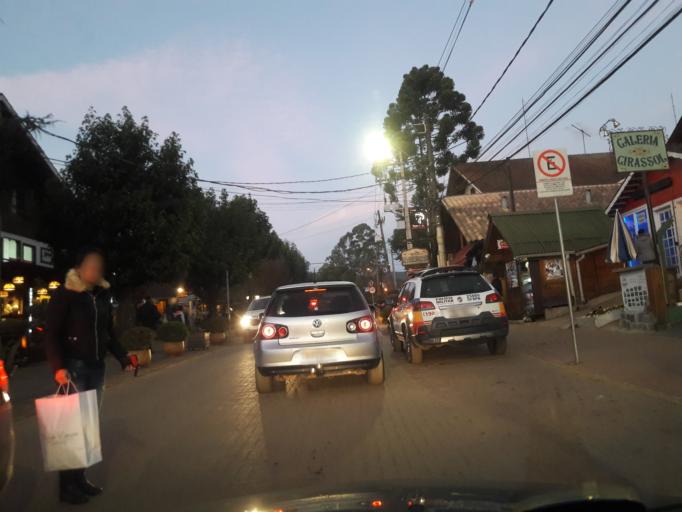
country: BR
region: Minas Gerais
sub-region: Camanducaia
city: Camanducaia
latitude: -22.8628
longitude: -46.0360
